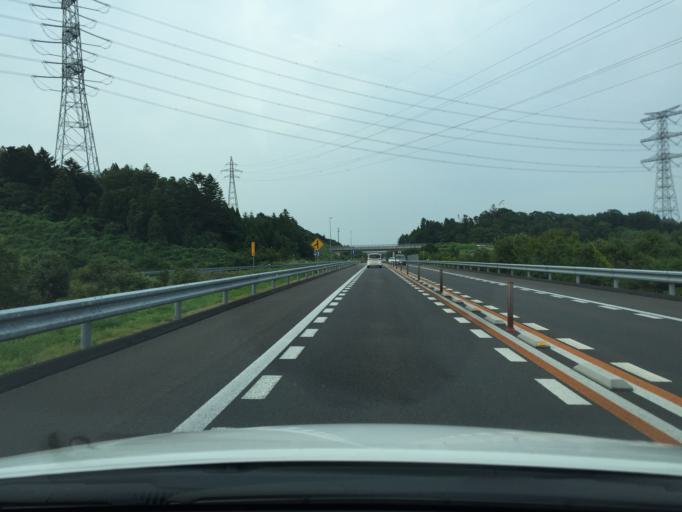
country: JP
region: Fukushima
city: Iwaki
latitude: 37.2370
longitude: 140.9831
